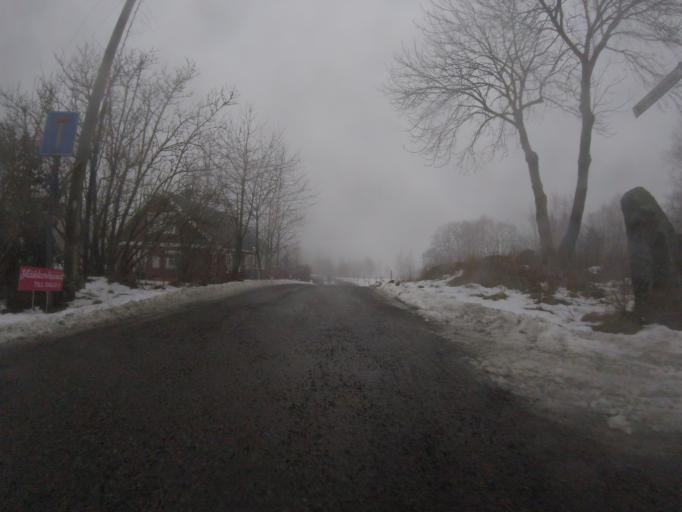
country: SE
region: Halland
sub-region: Varbergs Kommun
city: Varberg
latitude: 57.1949
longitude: 12.2131
